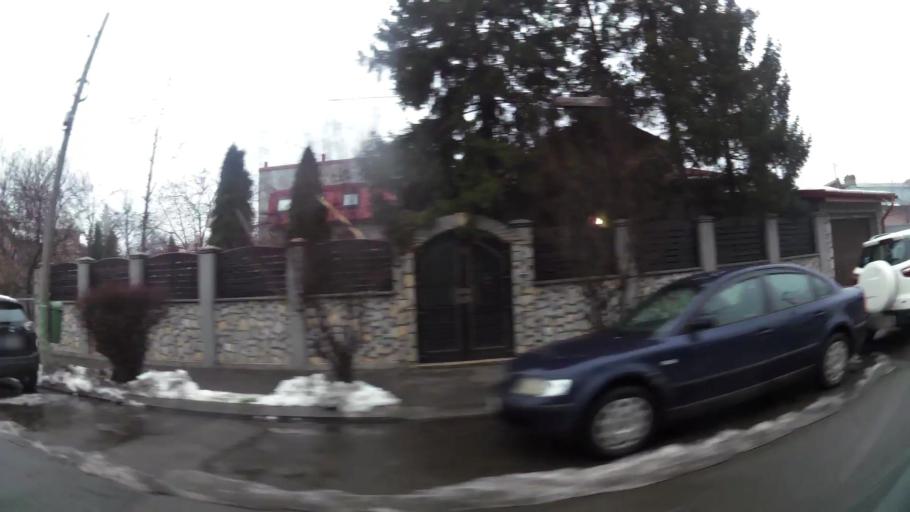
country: RO
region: Ilfov
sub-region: Comuna Chiajna
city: Rosu
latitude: 44.4837
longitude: 26.0332
